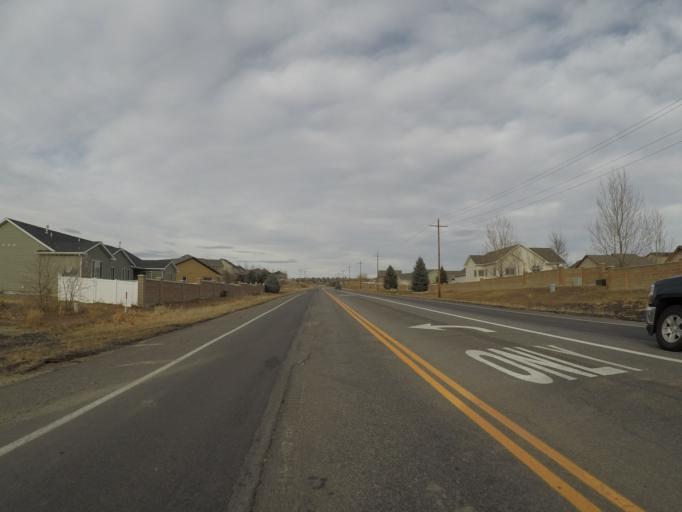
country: US
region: Montana
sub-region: Yellowstone County
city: Laurel
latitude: 45.8026
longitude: -108.6737
